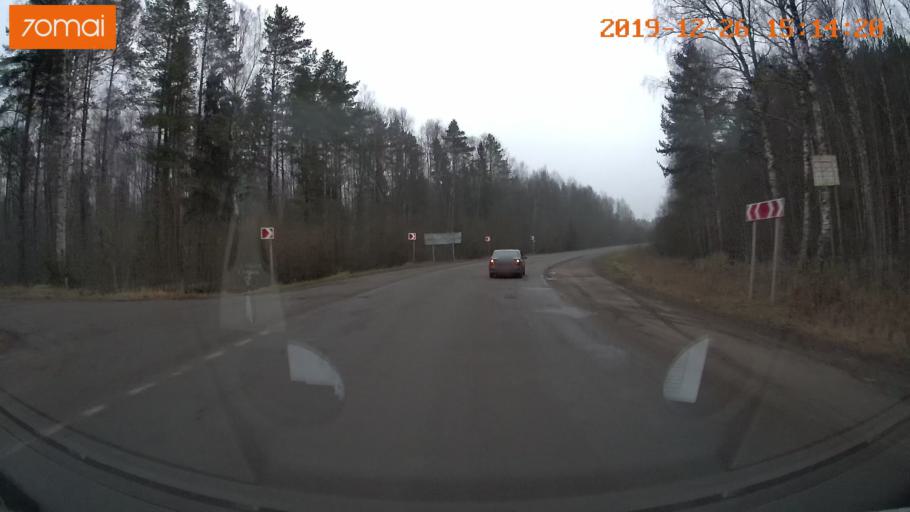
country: RU
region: Jaroslavl
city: Rybinsk
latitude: 58.1070
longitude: 38.8813
